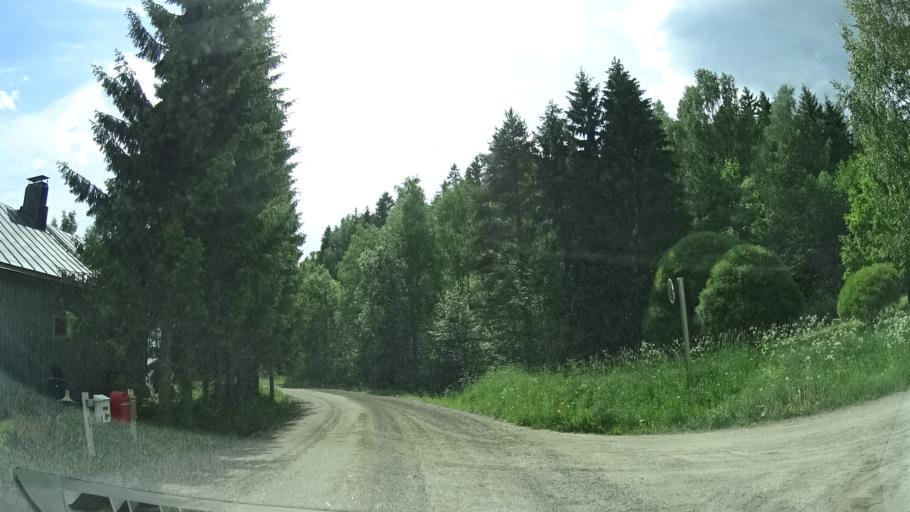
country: FI
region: Uusimaa
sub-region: Helsinki
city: Siuntio
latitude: 60.2020
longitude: 24.2576
